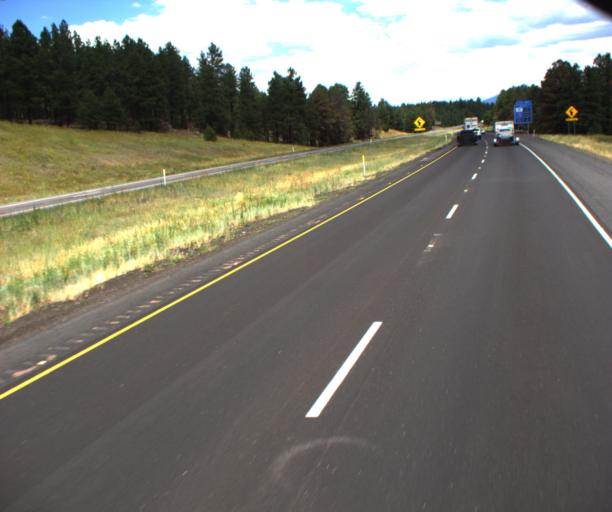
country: US
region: Arizona
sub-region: Coconino County
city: Kachina Village
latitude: 35.1065
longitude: -111.6810
